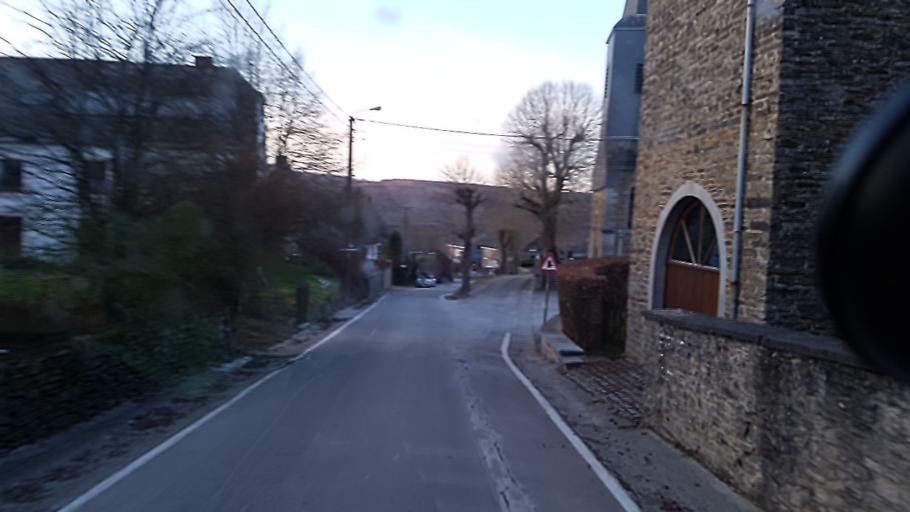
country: BE
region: Wallonia
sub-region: Province du Luxembourg
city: Daverdisse
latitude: 50.0207
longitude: 5.1183
